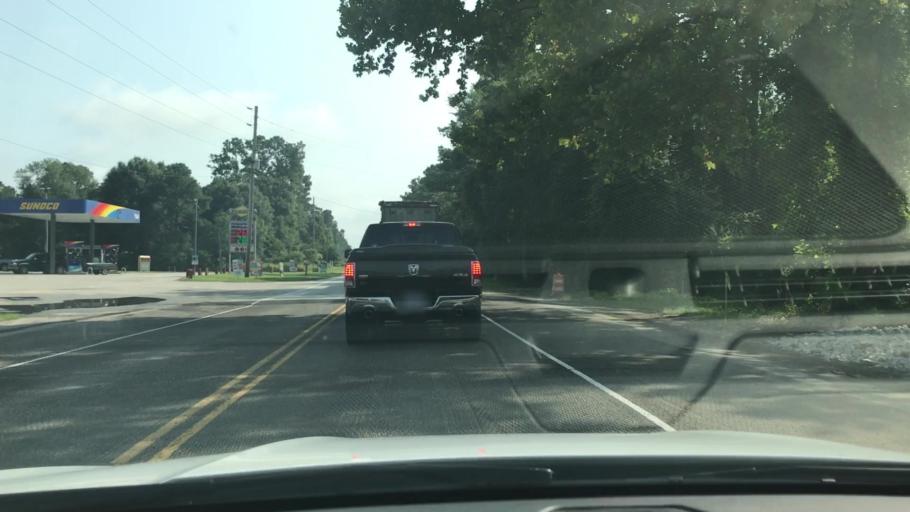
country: US
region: South Carolina
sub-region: Horry County
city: Socastee
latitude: 33.6712
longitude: -79.1390
